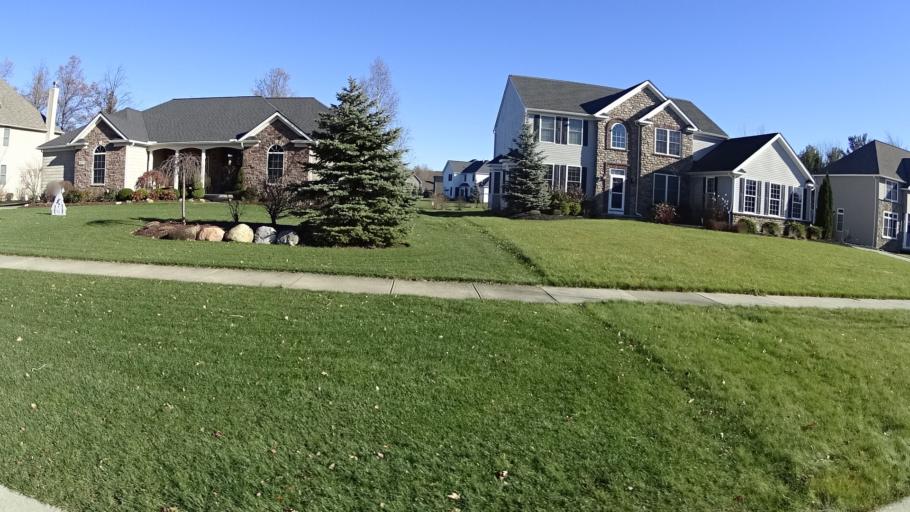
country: US
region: Ohio
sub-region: Lorain County
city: Avon Center
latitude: 41.4440
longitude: -81.9830
